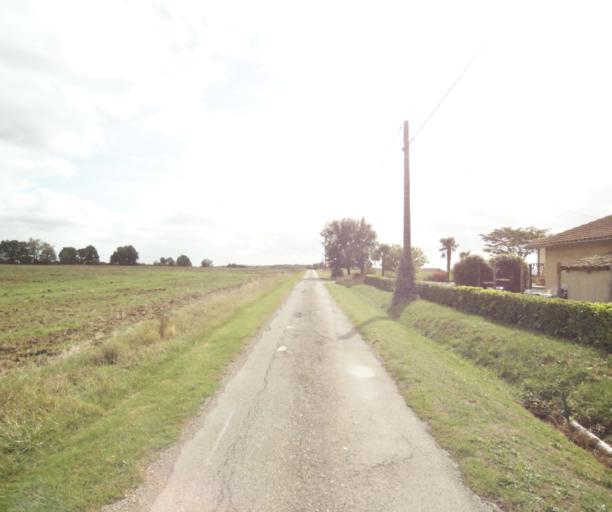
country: FR
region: Midi-Pyrenees
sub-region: Departement du Tarn-et-Garonne
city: Finhan
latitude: 43.8857
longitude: 1.1329
